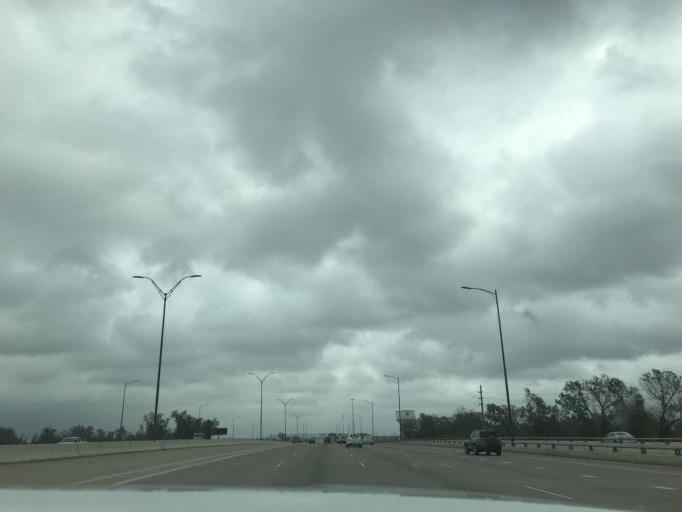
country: US
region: Texas
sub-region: Fort Bend County
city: Greatwood
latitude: 29.5676
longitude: -95.6687
